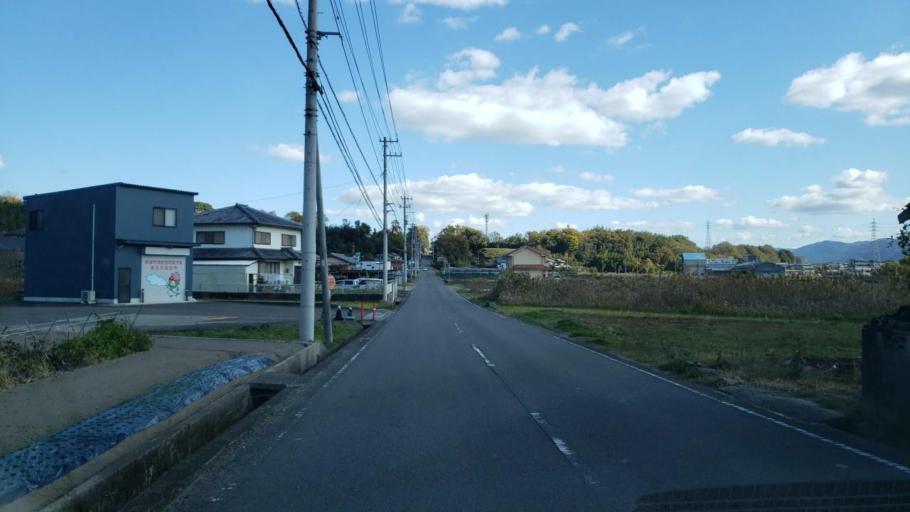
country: JP
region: Tokushima
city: Wakimachi
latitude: 34.0811
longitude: 134.2083
